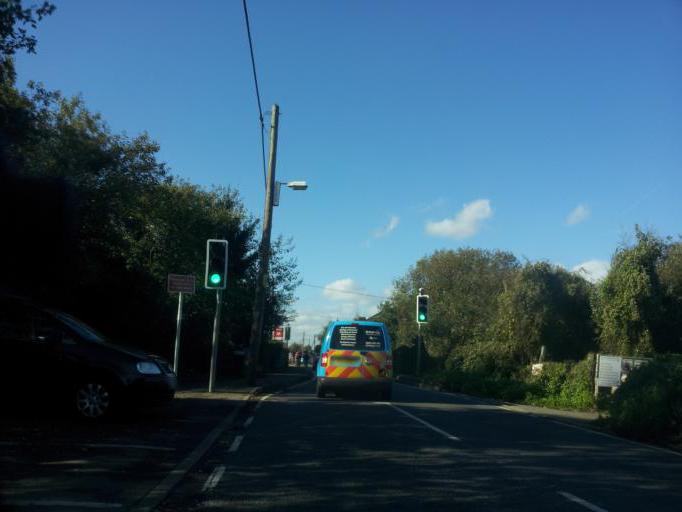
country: GB
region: England
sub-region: Kent
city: Rainham
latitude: 51.3751
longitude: 0.6160
